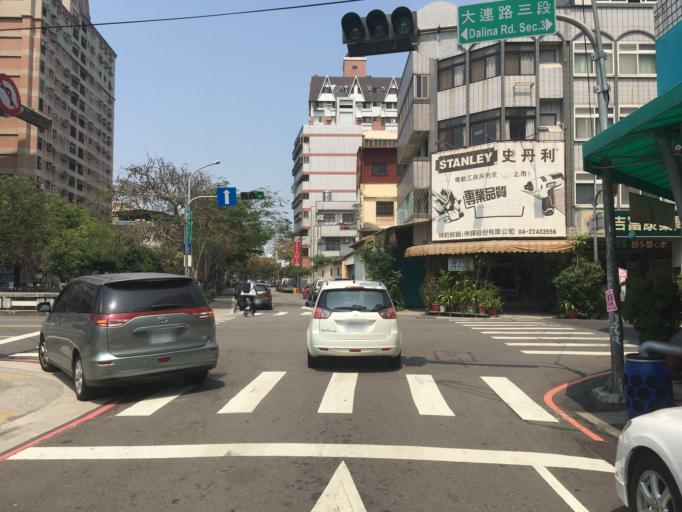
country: TW
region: Taiwan
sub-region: Taichung City
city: Taichung
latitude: 24.1747
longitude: 120.6933
